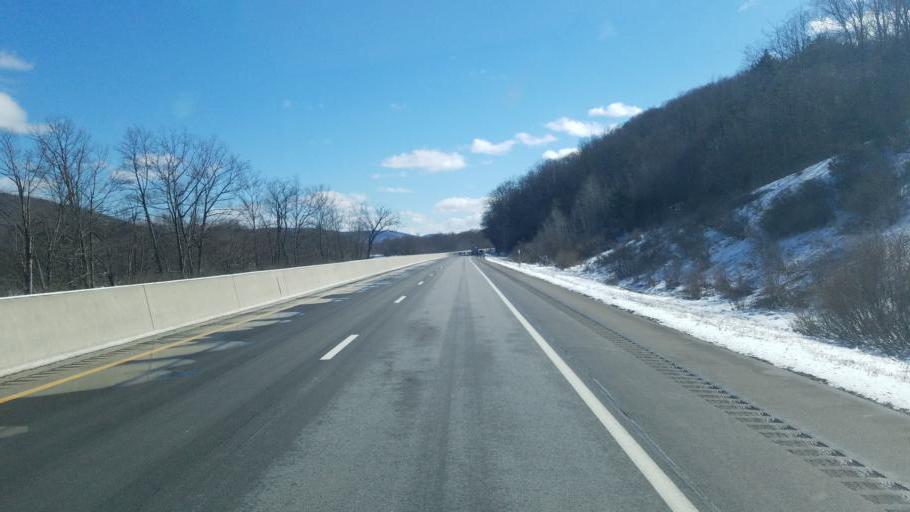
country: US
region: New York
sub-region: Cattaraugus County
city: Salamanca
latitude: 42.1225
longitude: -78.6652
